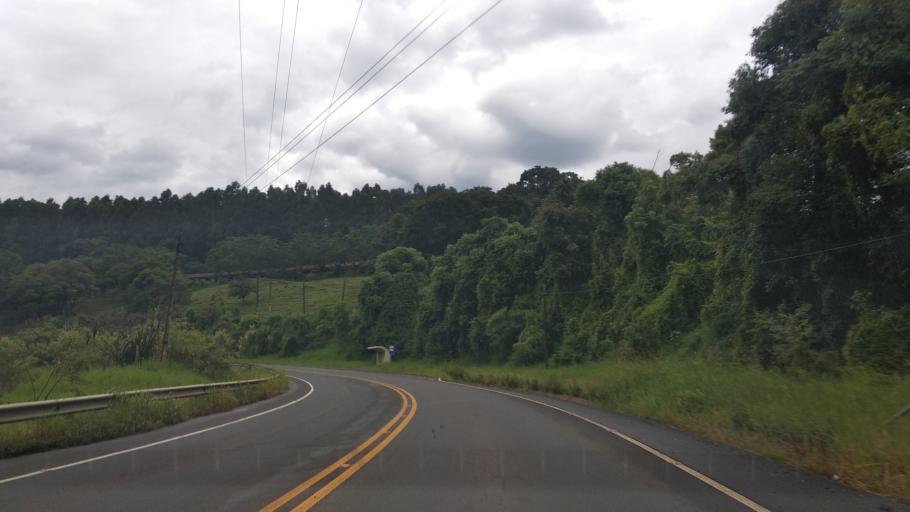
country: BR
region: Santa Catarina
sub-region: Videira
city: Videira
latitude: -27.0650
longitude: -51.2377
